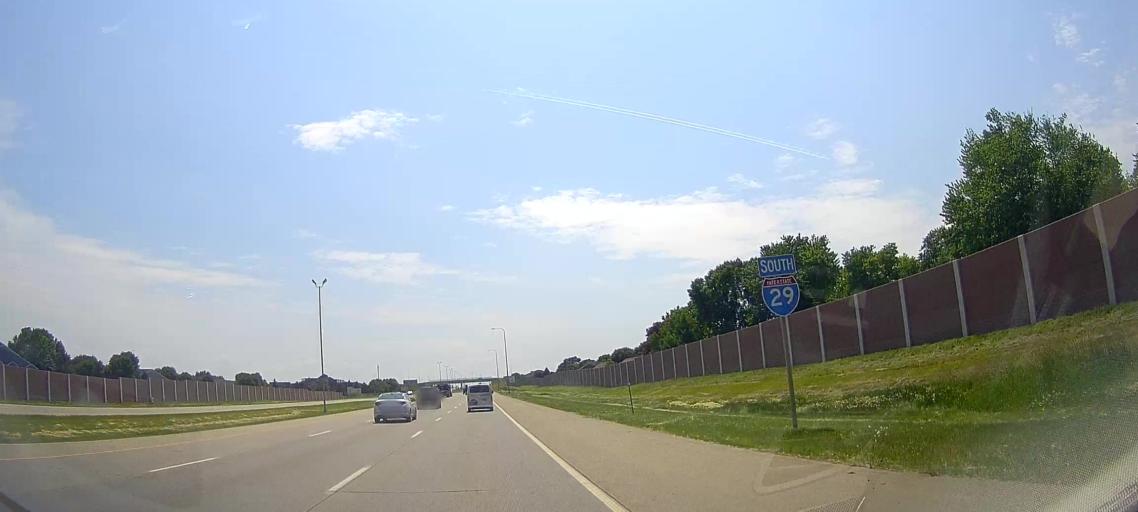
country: US
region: South Dakota
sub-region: Lincoln County
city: Tea
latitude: 43.5056
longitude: -96.7849
